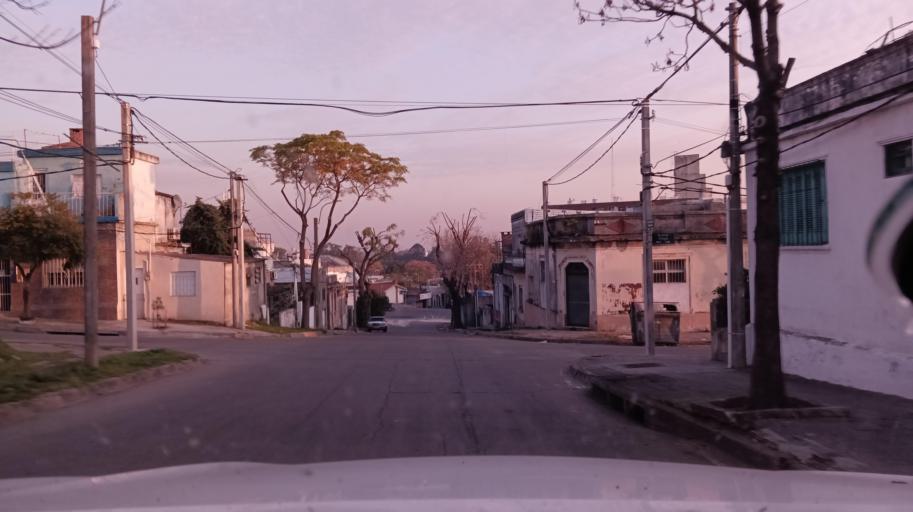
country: UY
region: Montevideo
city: Montevideo
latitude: -34.8583
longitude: -56.1734
